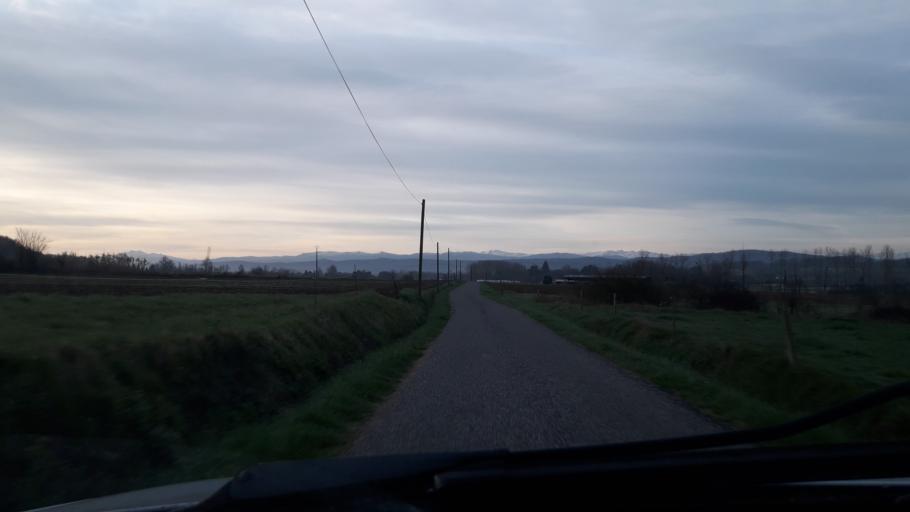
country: FR
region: Midi-Pyrenees
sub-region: Departement de la Haute-Garonne
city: Montesquieu-Volvestre
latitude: 43.1782
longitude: 1.2672
